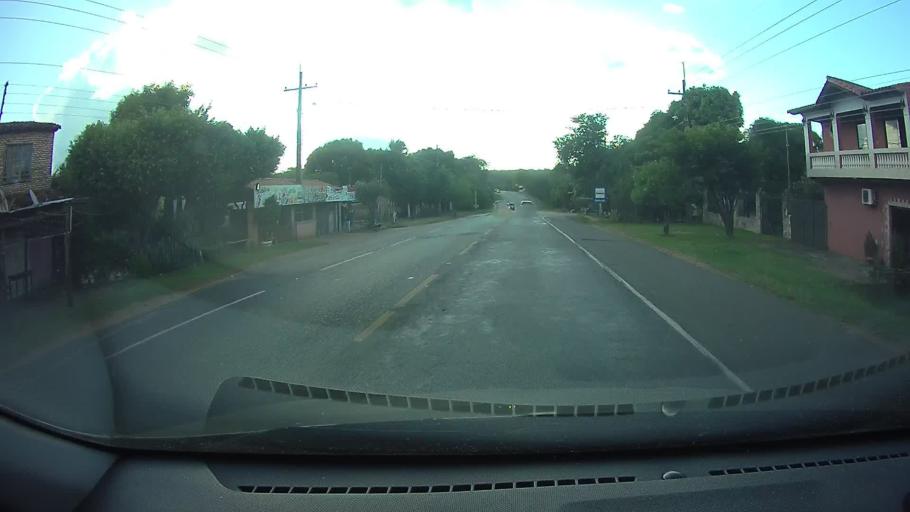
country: PY
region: Cordillera
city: Eusebio Ayala
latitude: -25.3774
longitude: -57.0238
